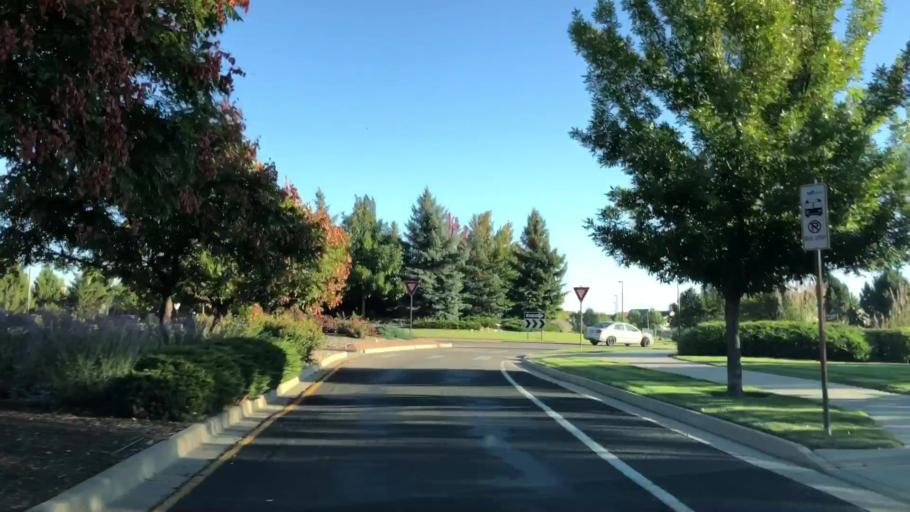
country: US
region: Colorado
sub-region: Larimer County
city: Loveland
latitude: 40.4098
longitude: -105.0114
